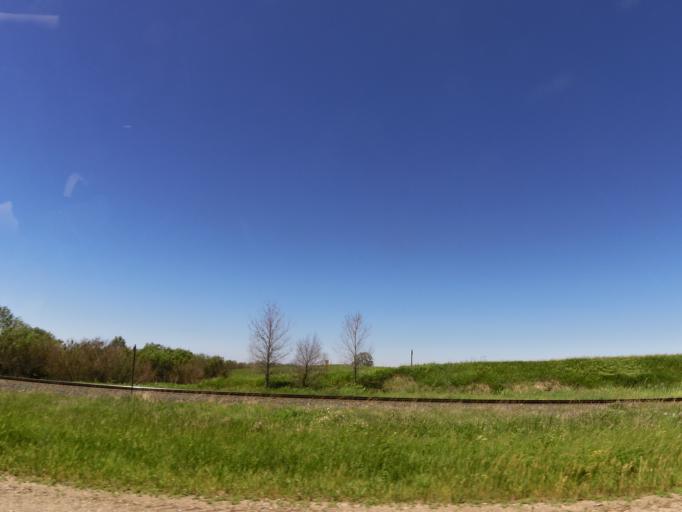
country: US
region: Minnesota
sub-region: Mahnomen County
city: Mahnomen
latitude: 47.0900
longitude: -95.9272
